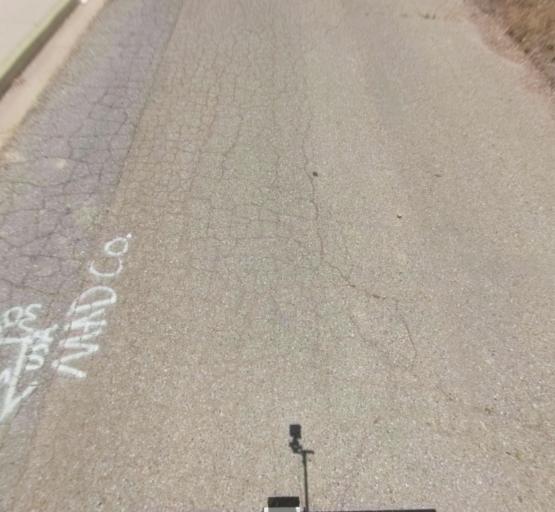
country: US
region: California
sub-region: Fresno County
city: Auberry
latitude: 37.2297
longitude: -119.5067
